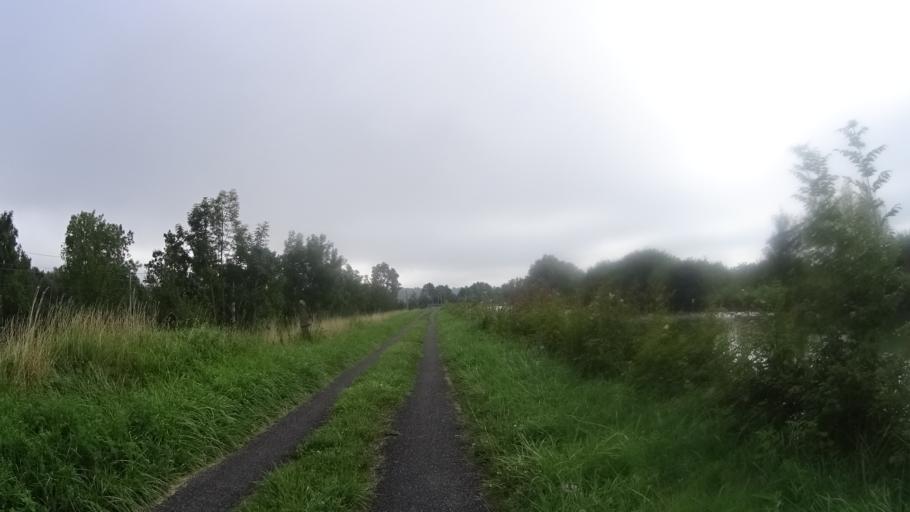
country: FR
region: Lorraine
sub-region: Departement de la Meuse
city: Fains-Veel
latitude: 48.8064
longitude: 5.0811
